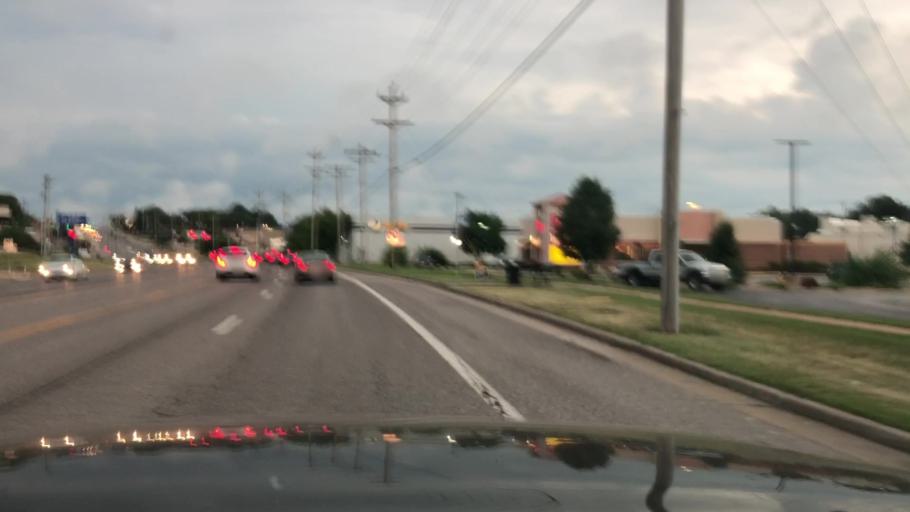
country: US
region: Missouri
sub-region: Saint Louis County
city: Bridgeton
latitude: 38.7477
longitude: -90.4225
